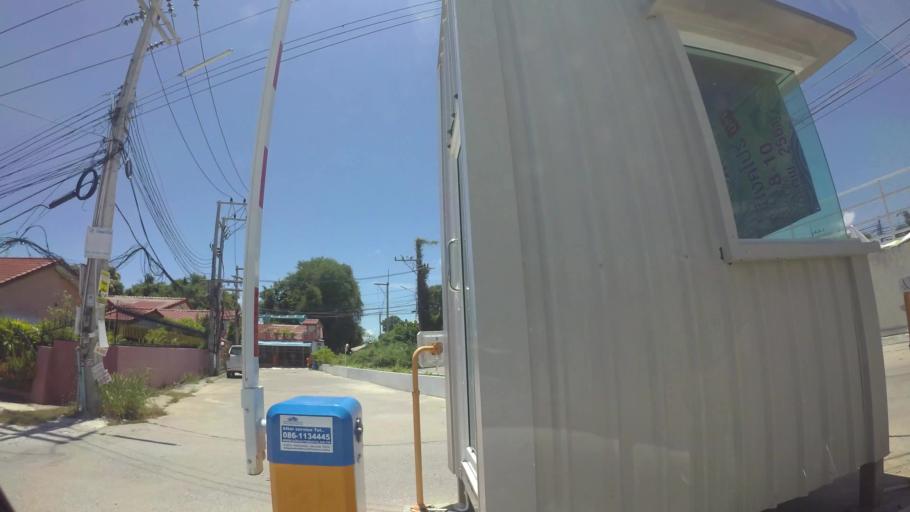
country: TH
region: Chon Buri
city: Phatthaya
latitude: 12.9226
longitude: 100.9025
